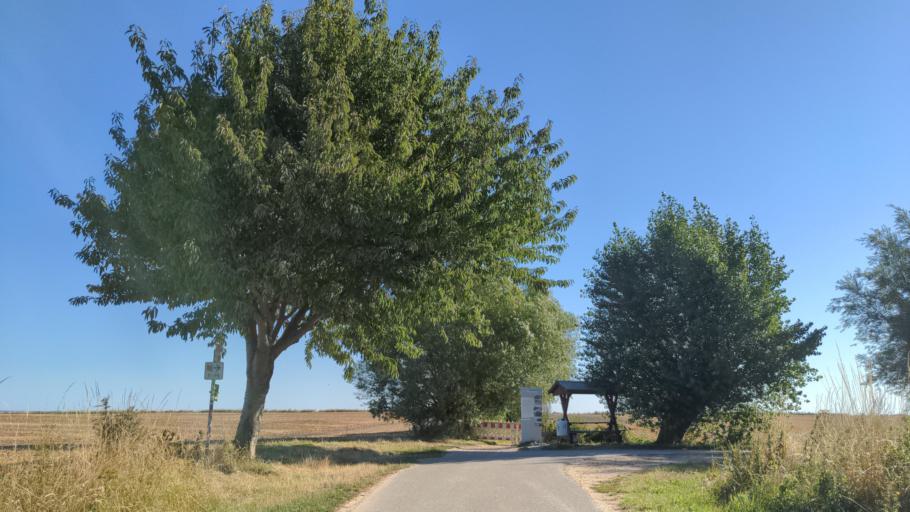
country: DE
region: Mecklenburg-Vorpommern
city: Ostseebad Boltenhagen
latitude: 54.0117
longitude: 11.1810
